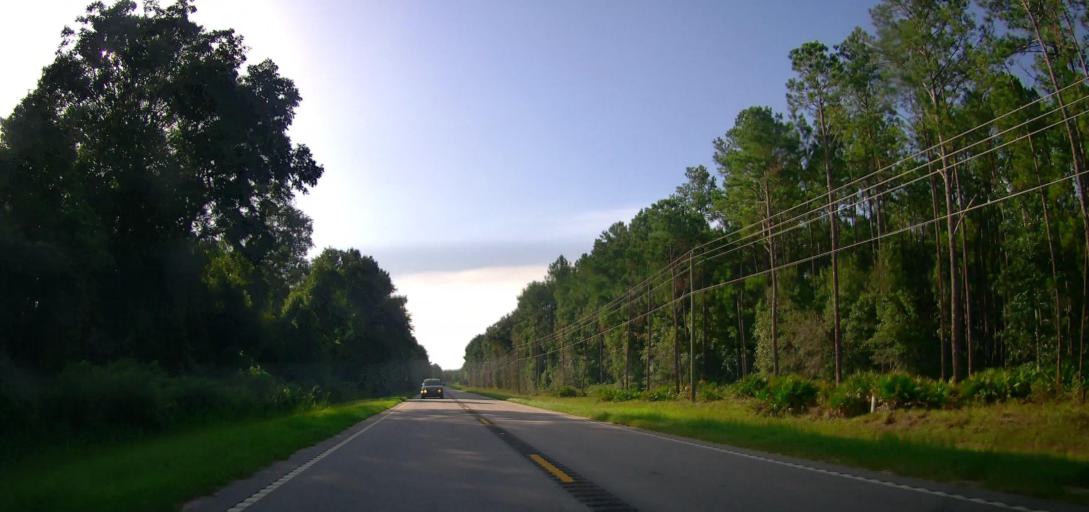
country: US
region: Georgia
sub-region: Coffee County
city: Nicholls
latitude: 31.3889
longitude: -82.6561
